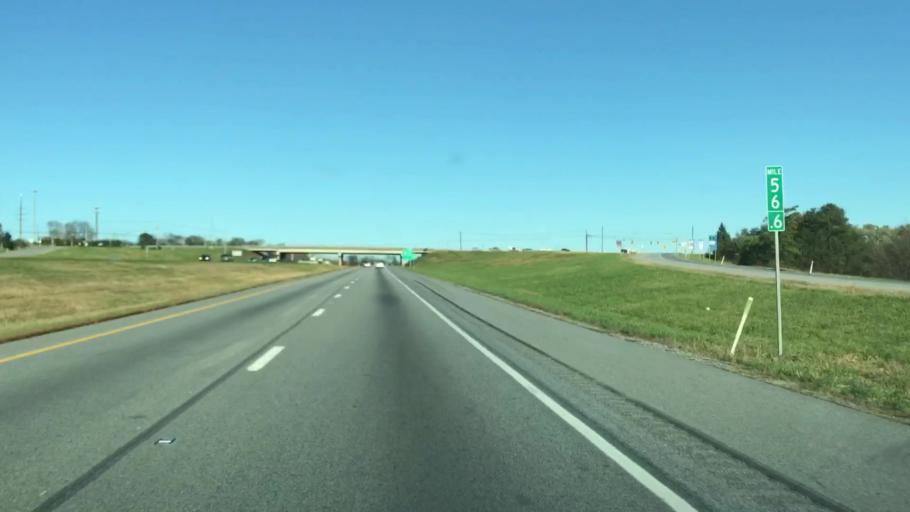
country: US
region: Pennsylvania
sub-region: Cumberland County
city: Mechanicsburg
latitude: 40.2668
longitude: -77.0482
